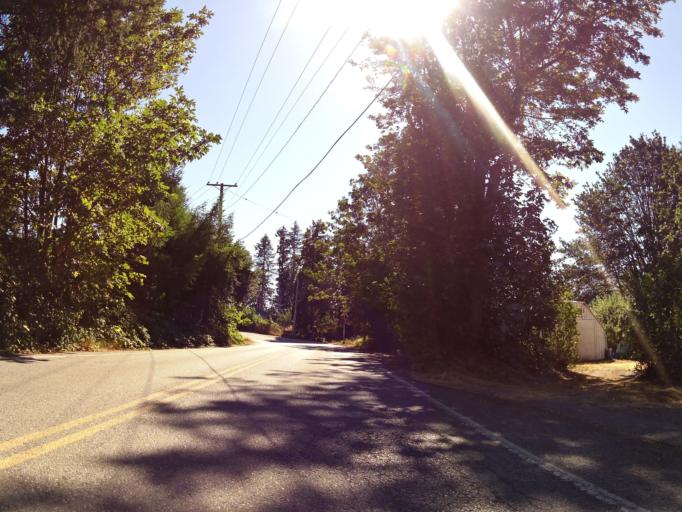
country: CA
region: British Columbia
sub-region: Cowichan Valley Regional District
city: Ladysmith
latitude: 48.9449
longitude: -123.7586
